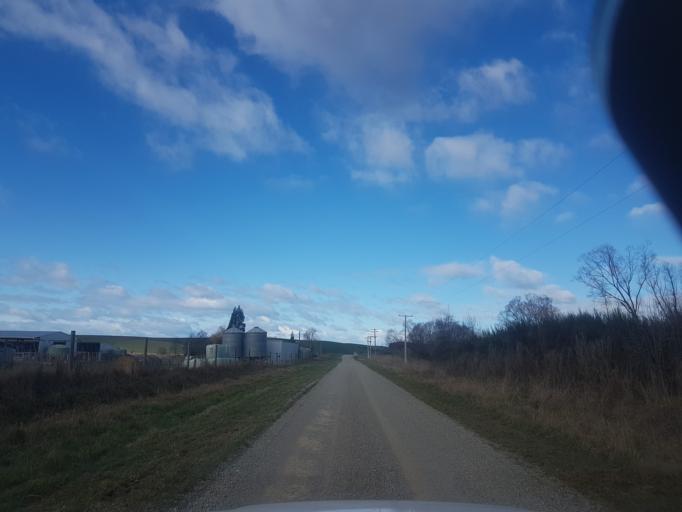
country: NZ
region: Canterbury
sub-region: Timaru District
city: Pleasant Point
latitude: -44.1914
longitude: 171.1998
